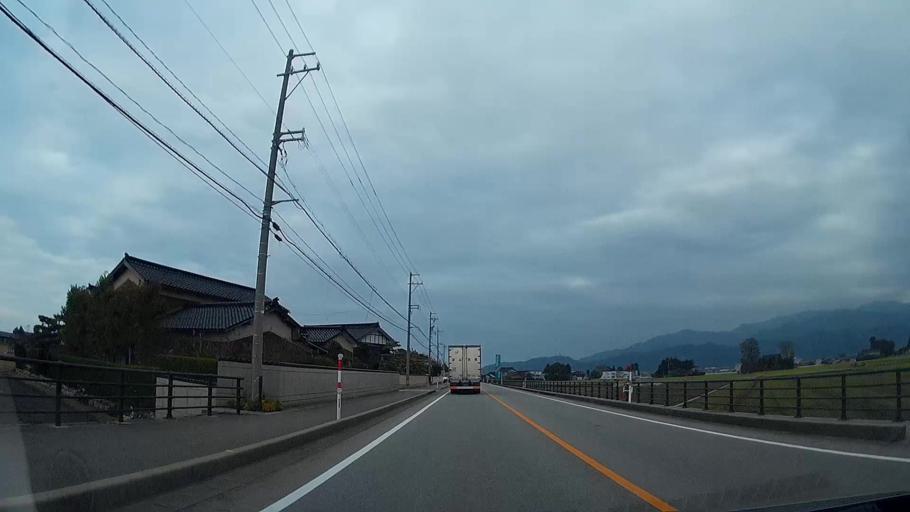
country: JP
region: Toyama
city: Nyuzen
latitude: 36.9424
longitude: 137.5205
